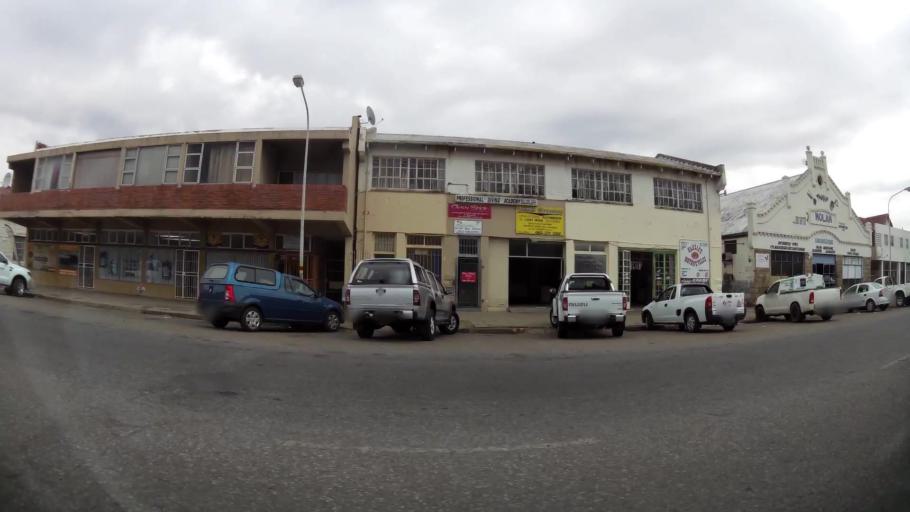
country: ZA
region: Orange Free State
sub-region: Fezile Dabi District Municipality
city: Kroonstad
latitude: -27.6673
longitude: 27.2337
